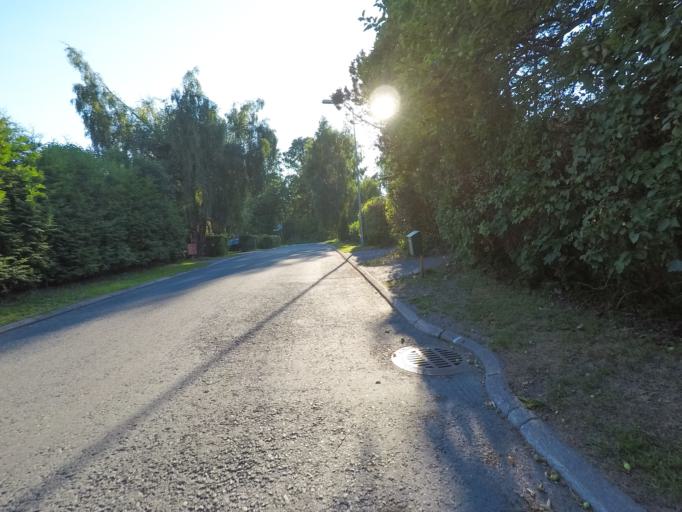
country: FI
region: Uusimaa
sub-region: Helsinki
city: Vantaa
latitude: 60.2145
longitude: 25.1094
